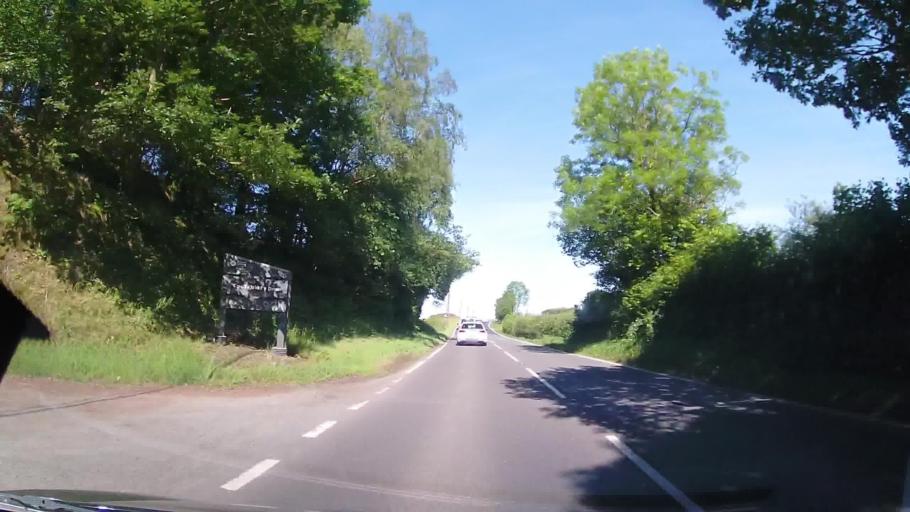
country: GB
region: Wales
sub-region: Sir Powys
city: Llangynog
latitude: 52.6734
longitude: -3.4102
